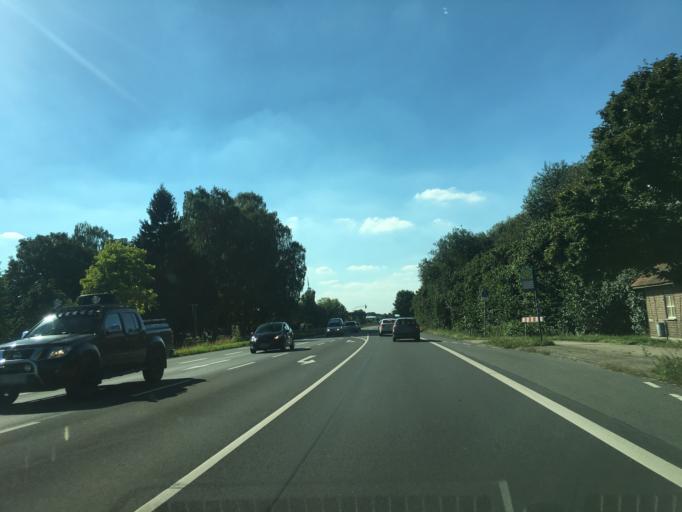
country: DE
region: North Rhine-Westphalia
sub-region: Regierungsbezirk Munster
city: Beelen
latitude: 51.9341
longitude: 8.1021
